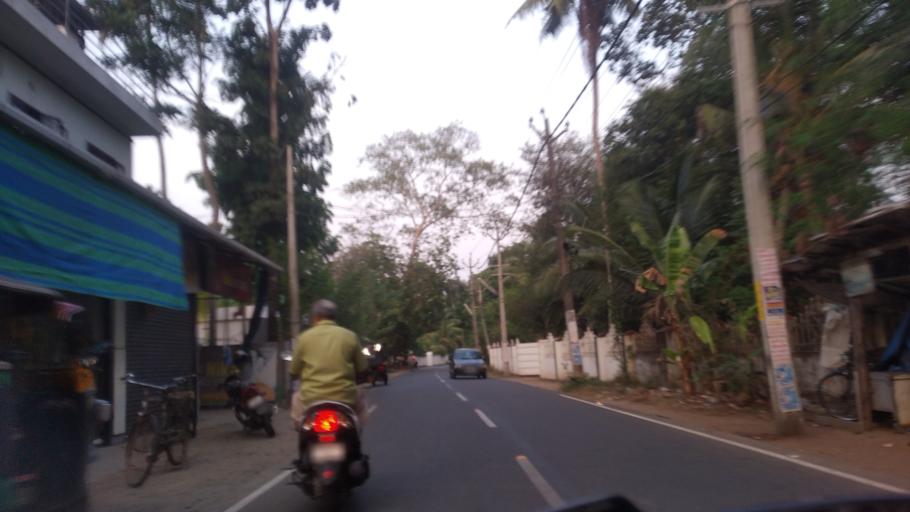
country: IN
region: Kerala
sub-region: Thrissur District
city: Kodungallur
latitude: 10.2063
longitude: 76.1819
